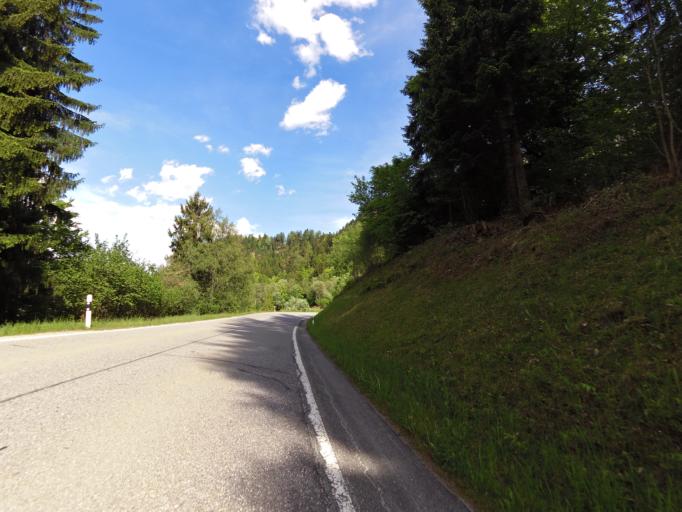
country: CH
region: Grisons
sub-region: Surselva District
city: Laax
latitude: 46.7916
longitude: 9.3063
